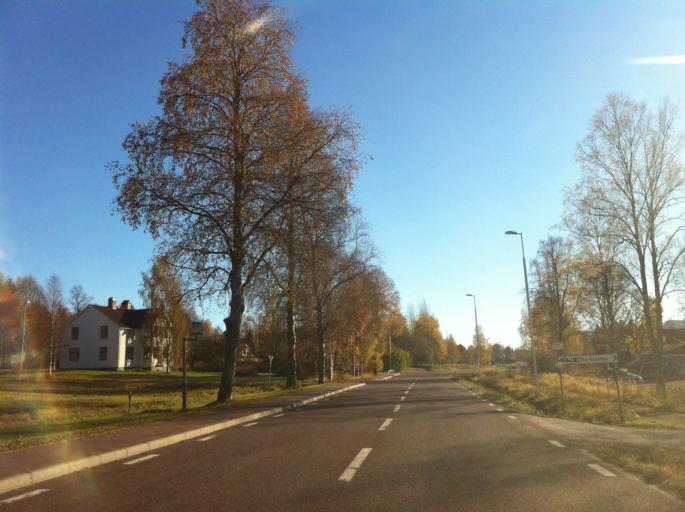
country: SE
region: Dalarna
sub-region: Alvdalens Kommun
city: AElvdalen
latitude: 61.2190
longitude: 14.0498
